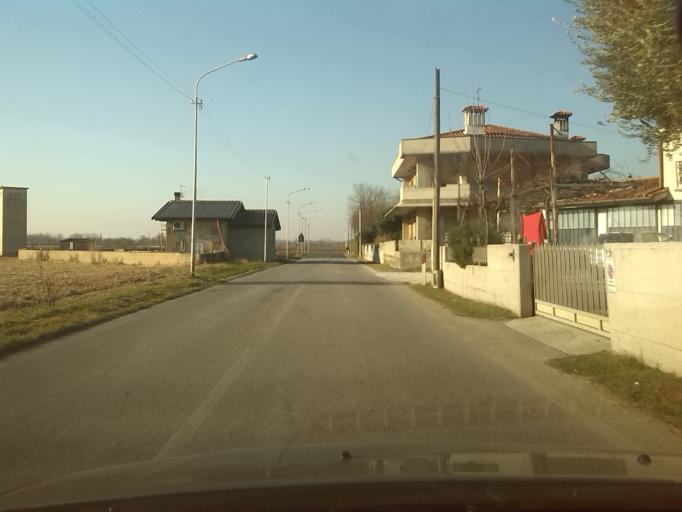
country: IT
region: Friuli Venezia Giulia
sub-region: Provincia di Udine
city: Percoto
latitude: 45.9814
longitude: 13.3448
